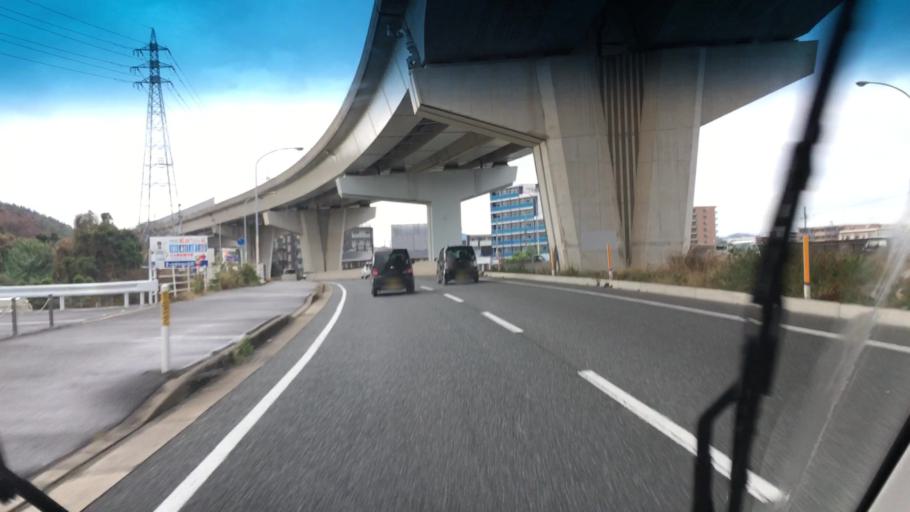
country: JP
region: Fukuoka
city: Maebaru-chuo
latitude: 33.5749
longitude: 130.2618
